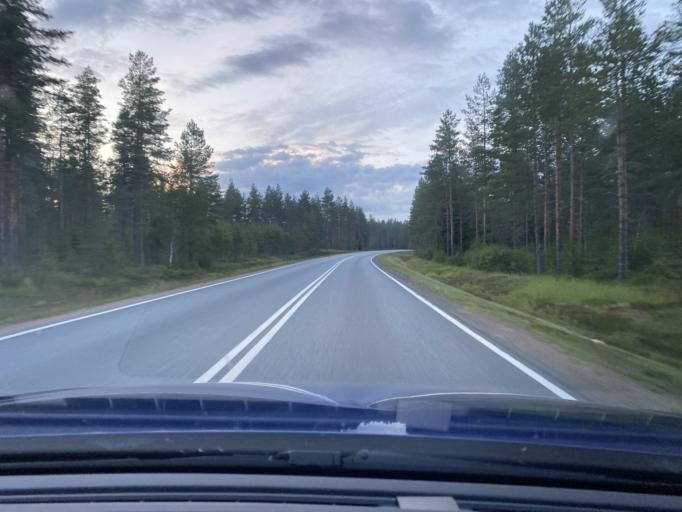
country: FI
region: Satakunta
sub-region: Pohjois-Satakunta
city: Honkajoki
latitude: 62.1265
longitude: 22.2452
